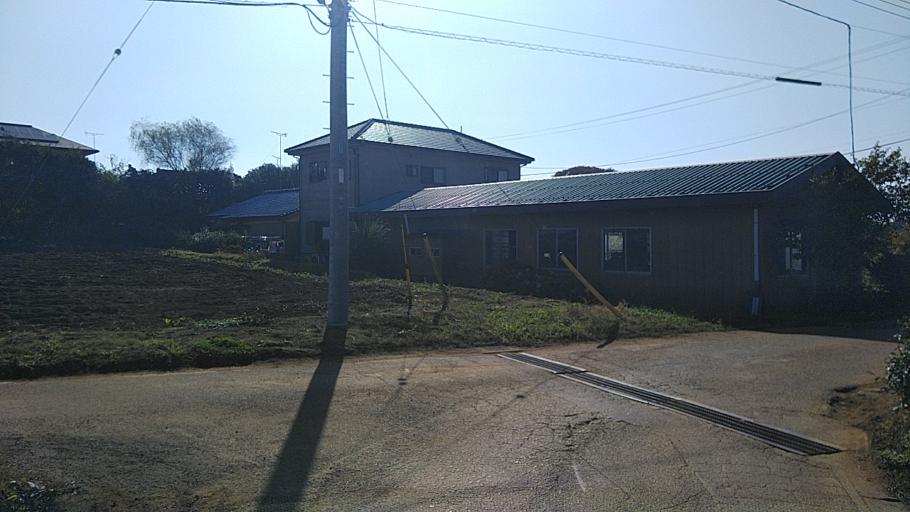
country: JP
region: Chiba
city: Sawara
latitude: 35.8371
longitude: 140.4682
